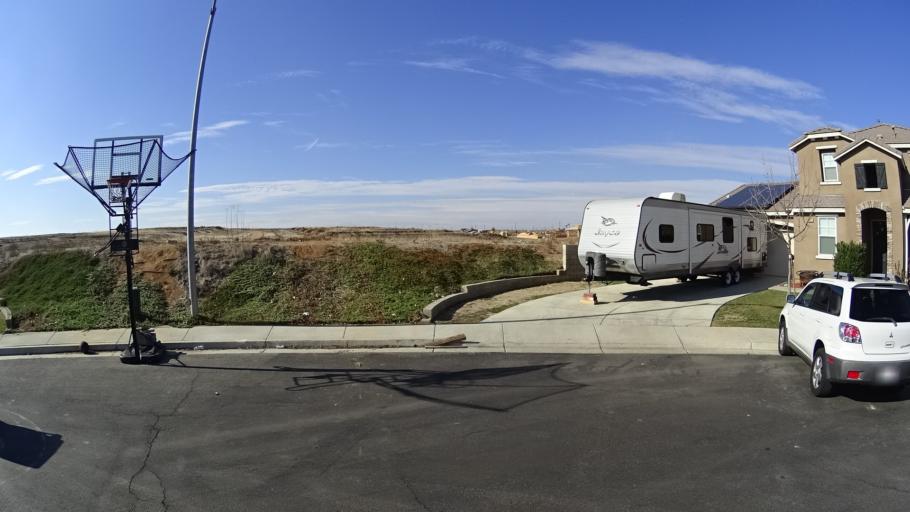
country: US
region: California
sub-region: Kern County
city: Oildale
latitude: 35.4098
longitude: -118.9007
